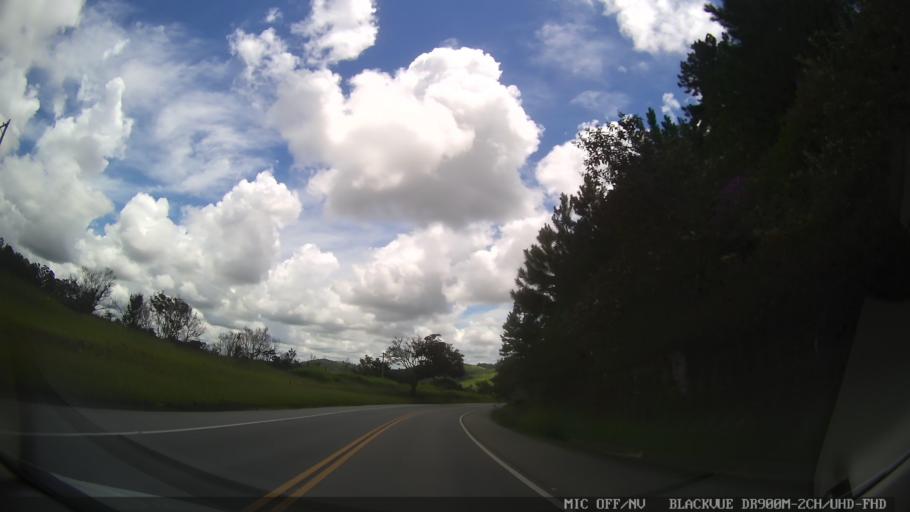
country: BR
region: Sao Paulo
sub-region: Amparo
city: Amparo
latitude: -22.7743
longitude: -46.7364
